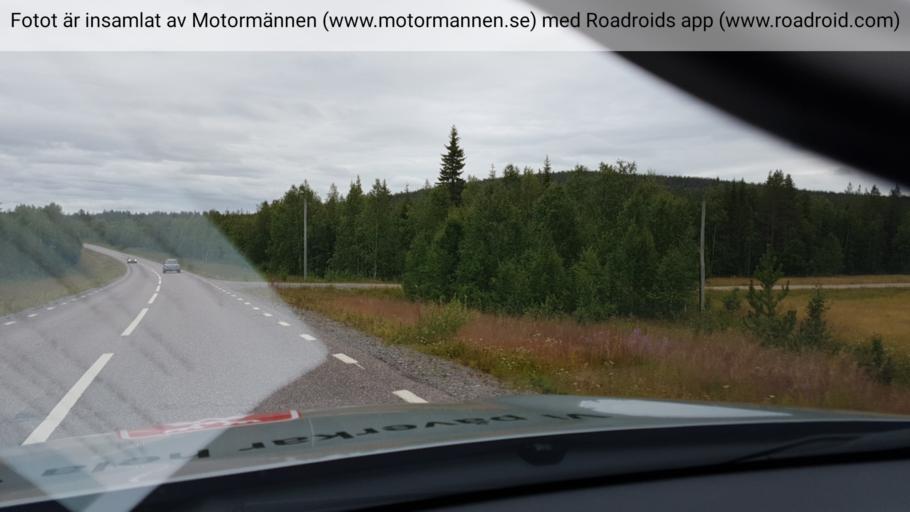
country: SE
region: Norrbotten
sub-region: Gallivare Kommun
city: Gaellivare
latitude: 67.0301
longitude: 21.7278
